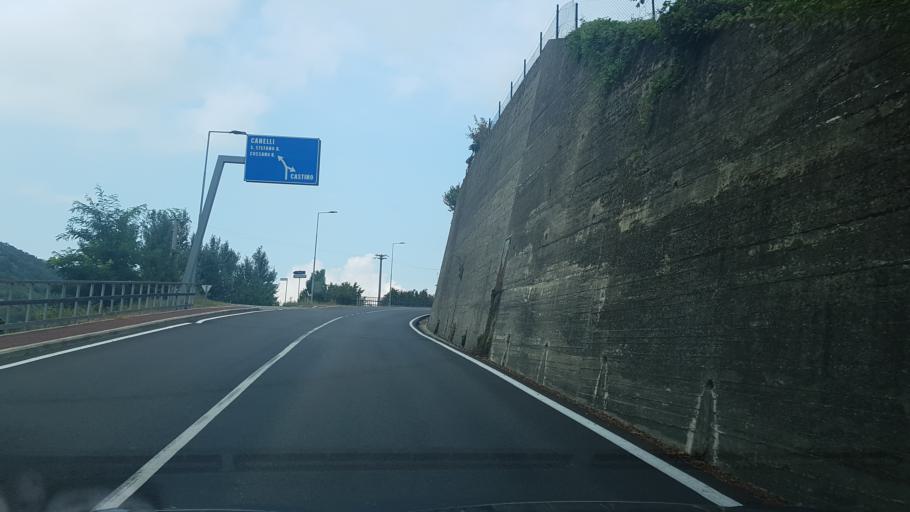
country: IT
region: Piedmont
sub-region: Provincia di Cuneo
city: Cossano Belbo
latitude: 44.6621
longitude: 8.1943
